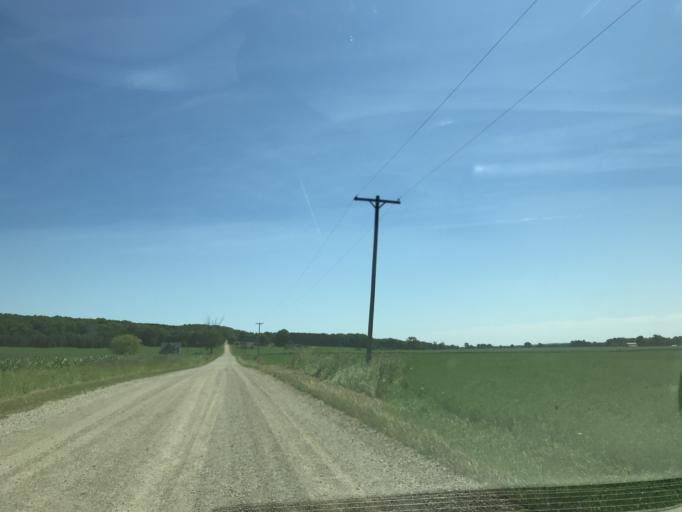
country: US
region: Michigan
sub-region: Missaukee County
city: Lake City
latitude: 44.2792
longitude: -85.0520
